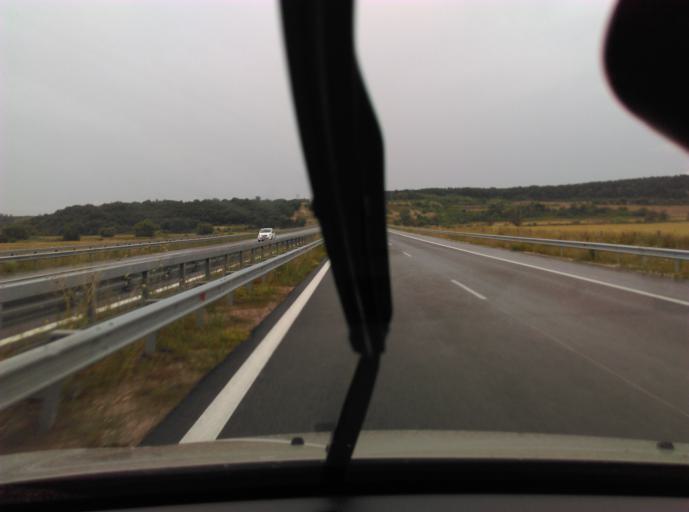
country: BG
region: Khaskovo
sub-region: Obshtina Dimitrovgrad
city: Dimitrovgrad
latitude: 42.0331
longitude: 25.5463
